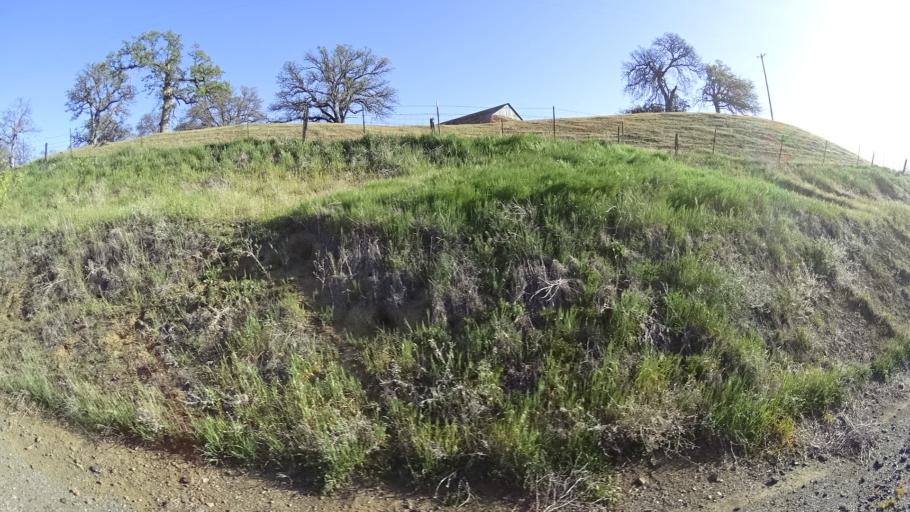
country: US
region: California
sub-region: Tehama County
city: Rancho Tehama Reserve
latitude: 39.7899
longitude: -122.5017
